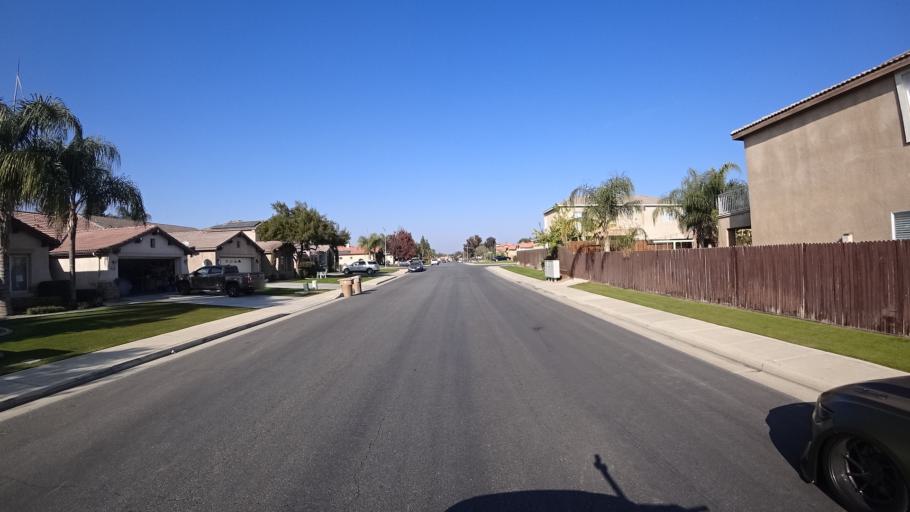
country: US
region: California
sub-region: Kern County
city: Rosedale
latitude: 35.3556
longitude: -119.1667
